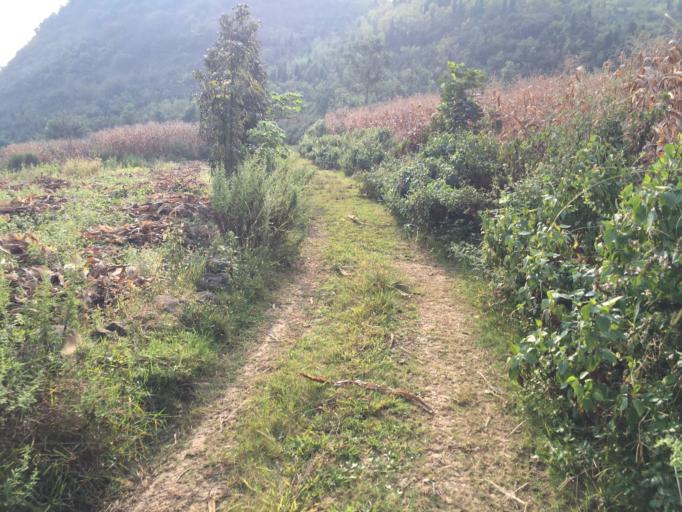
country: CN
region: Guangxi Zhuangzu Zizhiqu
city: Xinzhou
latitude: 25.4412
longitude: 105.6358
